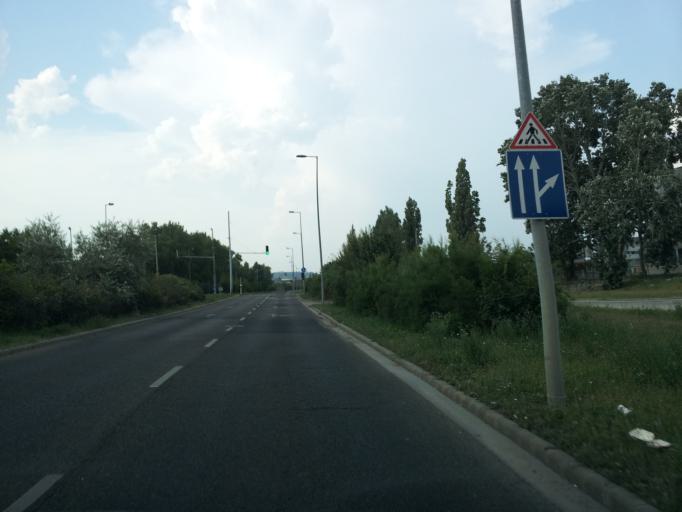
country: HU
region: Budapest
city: Budapest XXII. keruelet
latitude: 47.4431
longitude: 19.0430
